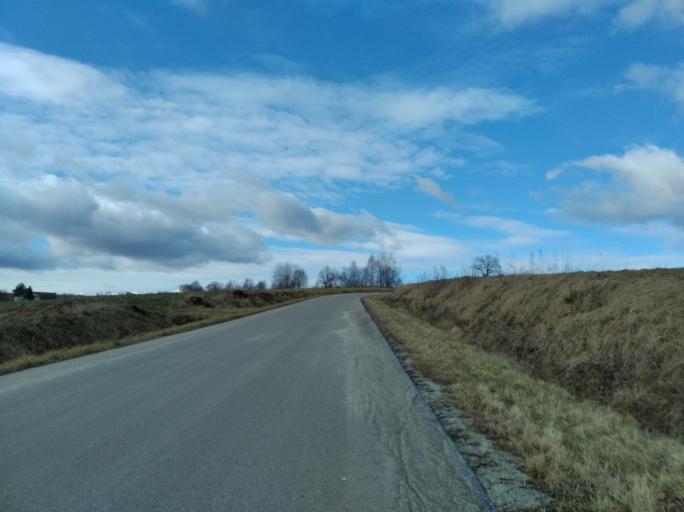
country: PL
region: Subcarpathian Voivodeship
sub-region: Powiat strzyzowski
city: Wisniowa
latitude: 49.9161
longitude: 21.6605
